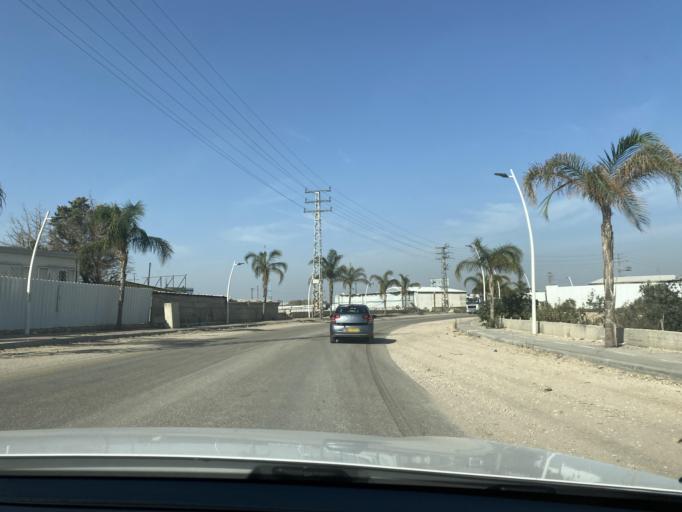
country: IL
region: Central District
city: Jaljulya
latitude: 32.1375
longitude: 34.9619
